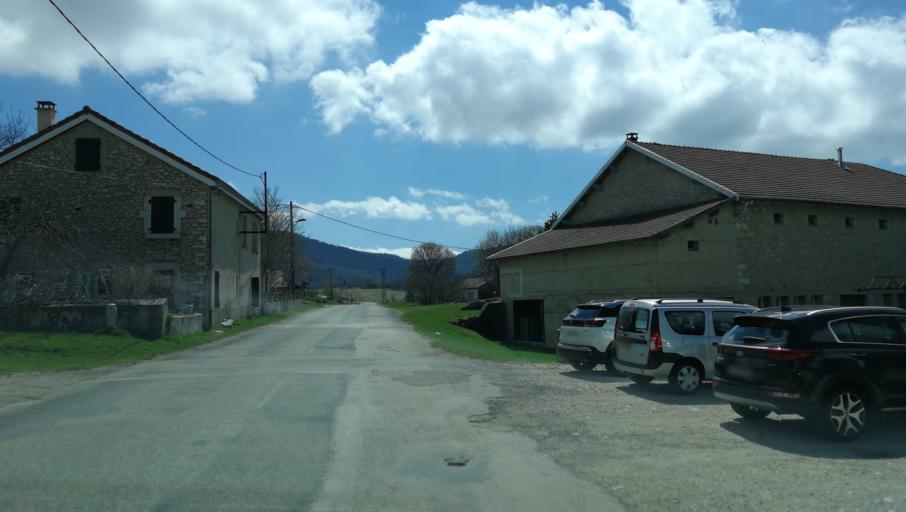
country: FR
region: Rhone-Alpes
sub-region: Departement de la Drome
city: Saint-Laurent-en-Royans
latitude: 44.8949
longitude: 5.3719
